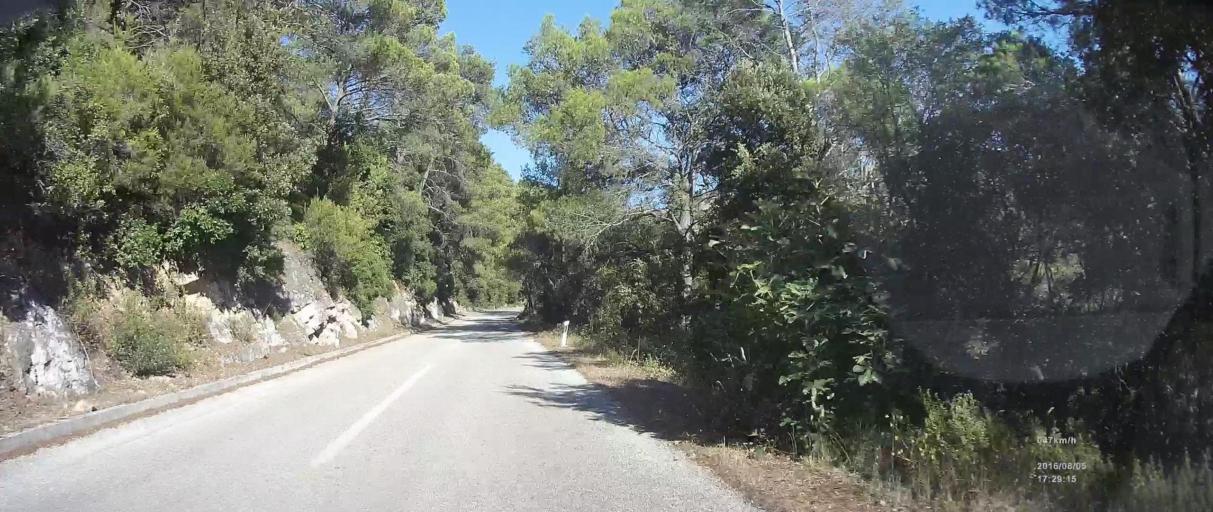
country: HR
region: Dubrovacko-Neretvanska
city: Blato
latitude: 42.7788
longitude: 17.4064
